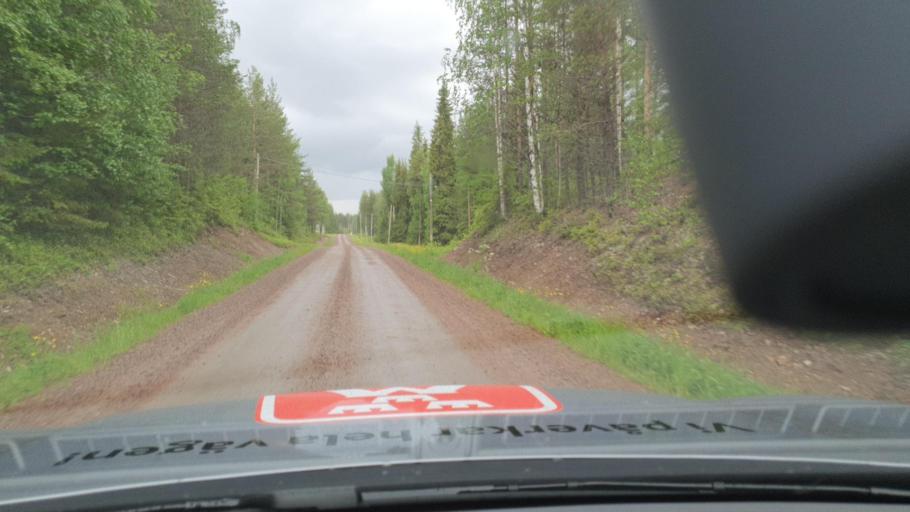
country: SE
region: Norrbotten
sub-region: Overkalix Kommun
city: OEverkalix
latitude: 66.6275
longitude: 22.7223
